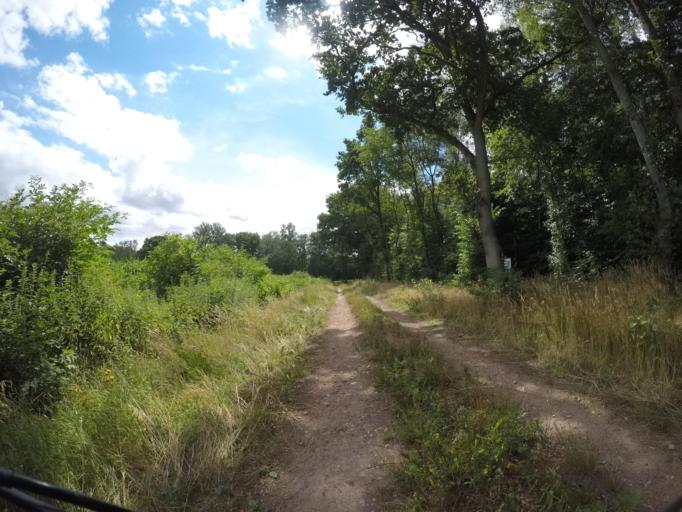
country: DE
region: Lower Saxony
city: Neu Darchau
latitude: 53.2881
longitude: 10.9662
